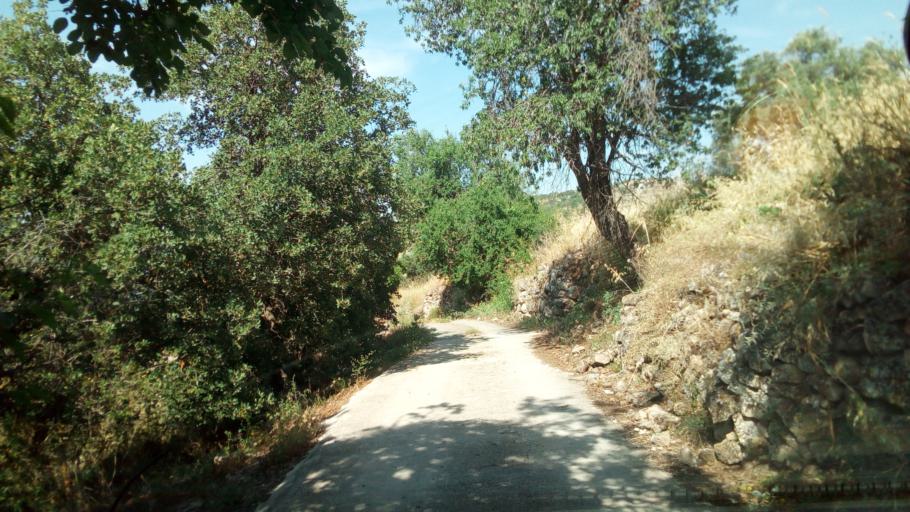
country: CY
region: Pafos
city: Tala
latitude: 34.9290
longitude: 32.5303
